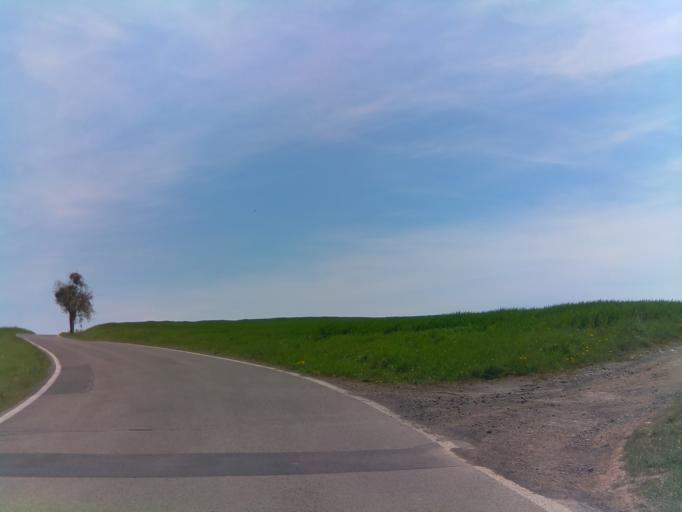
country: DE
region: Thuringia
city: Veilsdorf
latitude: 50.3576
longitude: 10.7702
